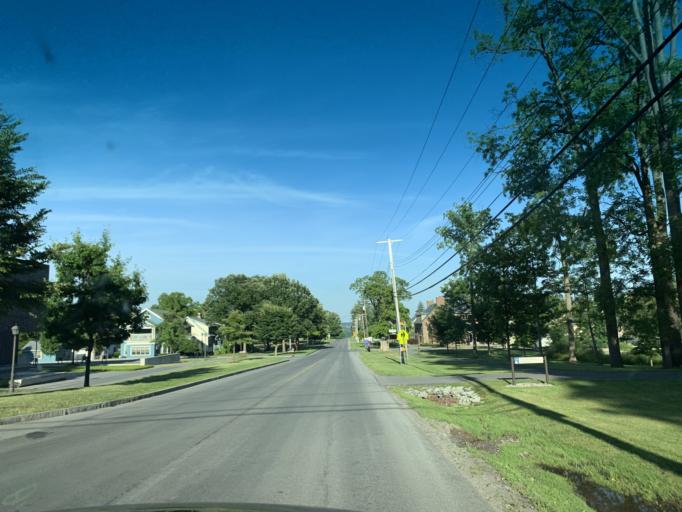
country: US
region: New York
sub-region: Oneida County
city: Clinton
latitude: 43.0507
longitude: -75.4102
